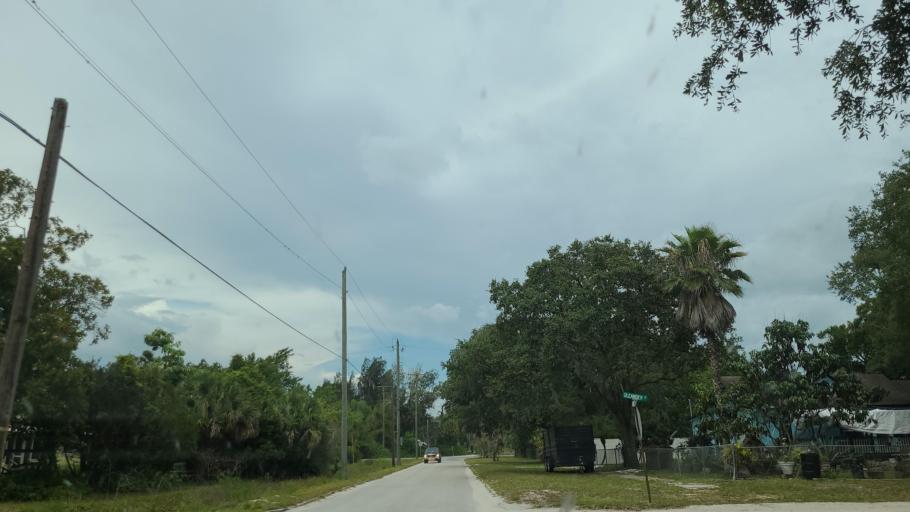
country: US
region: Florida
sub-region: Indian River County
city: Fellsmere
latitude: 27.7718
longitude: -80.6070
